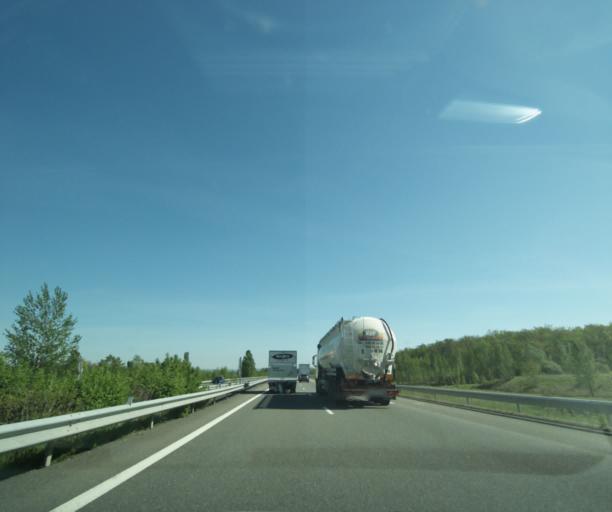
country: FR
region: Midi-Pyrenees
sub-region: Departement du Tarn-et-Garonne
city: Caussade
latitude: 44.2399
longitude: 1.5224
